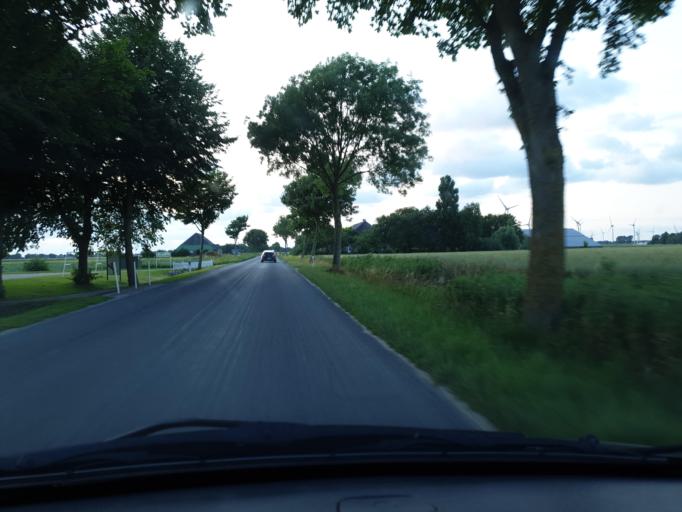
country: DE
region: Schleswig-Holstein
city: Kronprinzenkoog
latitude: 53.9626
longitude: 8.9315
